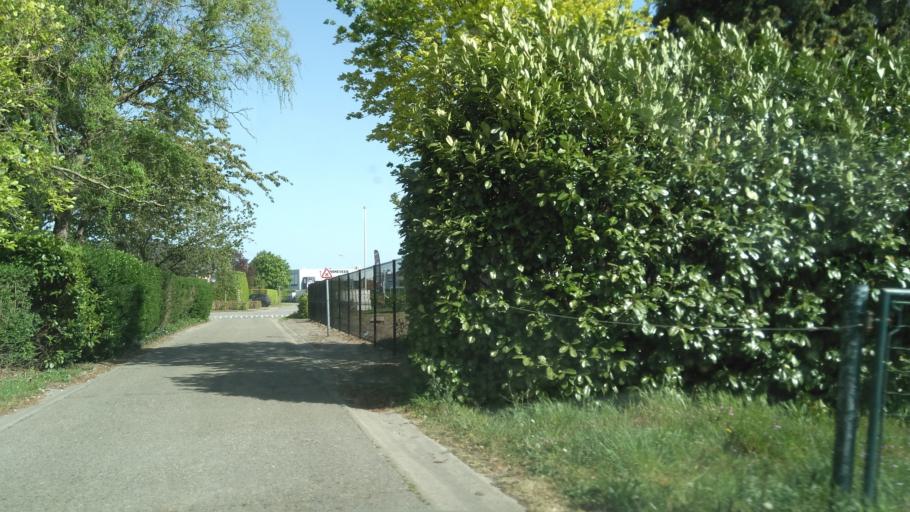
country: NL
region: North Brabant
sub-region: Gemeente Baarle-Nassau
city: Baarle-Nassau
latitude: 51.4339
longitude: 4.9354
